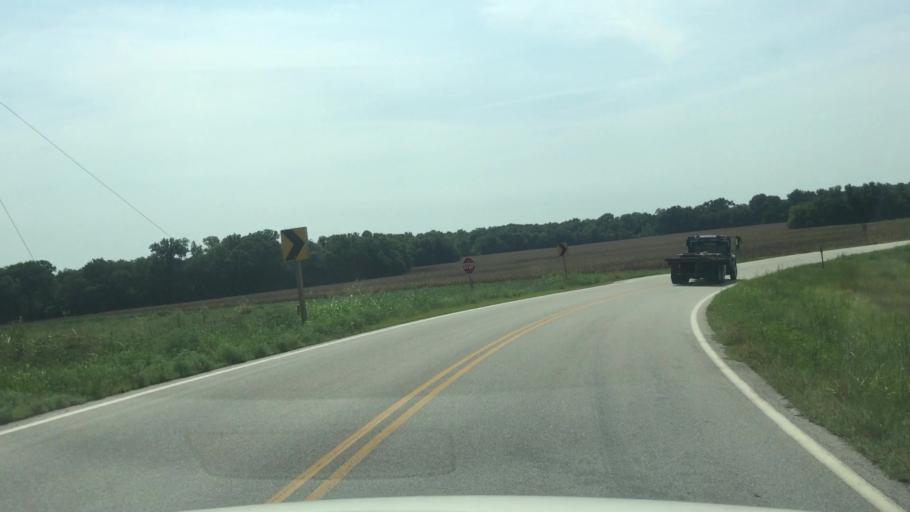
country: US
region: Kansas
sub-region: Montgomery County
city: Cherryvale
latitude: 37.2074
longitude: -95.5579
